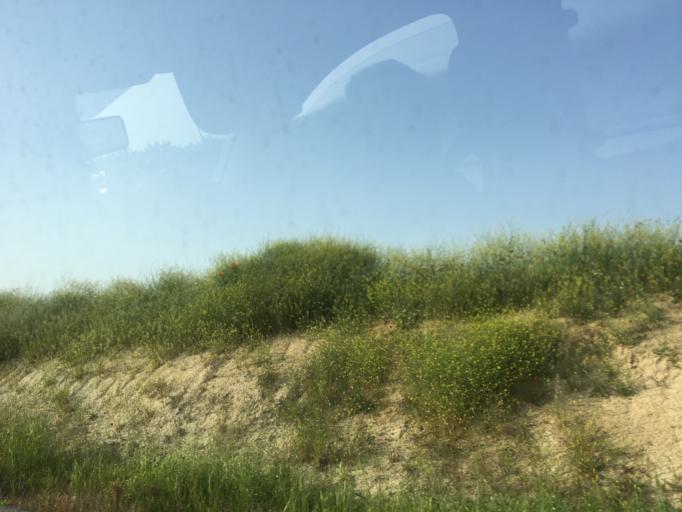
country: TR
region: Manisa
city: Ahmetli
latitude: 38.5660
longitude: 28.0357
